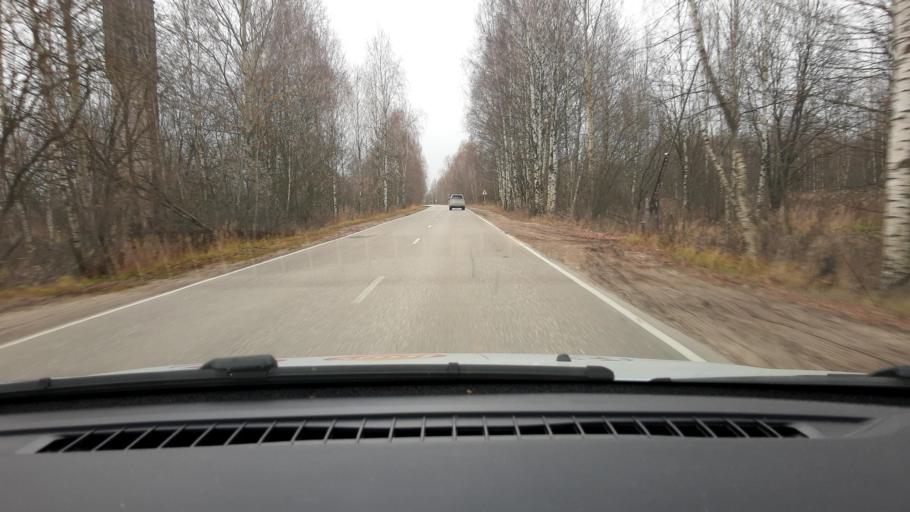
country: RU
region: Nizjnij Novgorod
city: Neklyudovo
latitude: 56.4721
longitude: 43.8862
